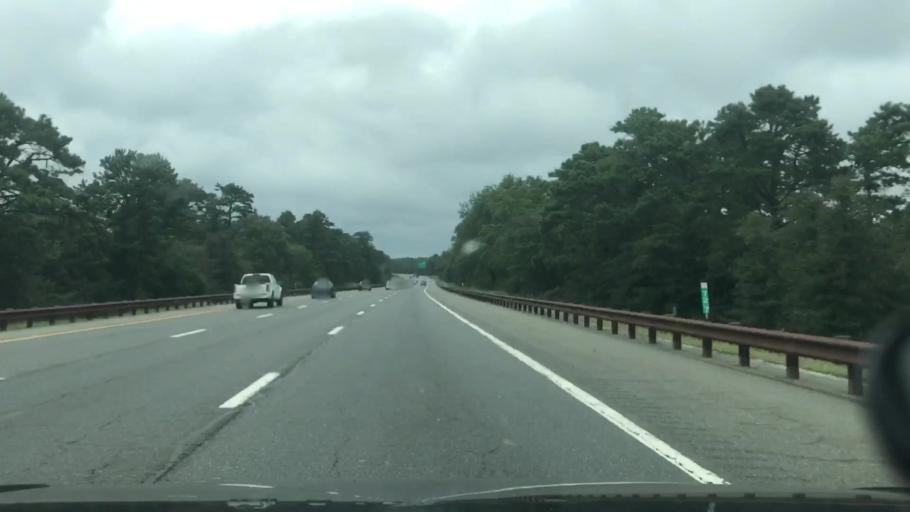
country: US
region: New Jersey
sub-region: Ocean County
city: Forked River
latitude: 39.8268
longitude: -74.2265
